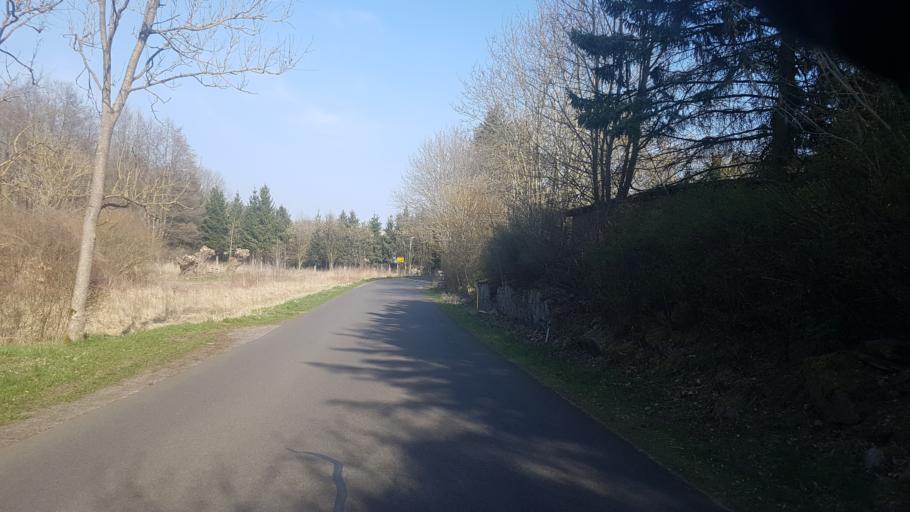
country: DE
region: Brandenburg
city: Gerswalde
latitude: 53.2154
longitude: 13.7940
